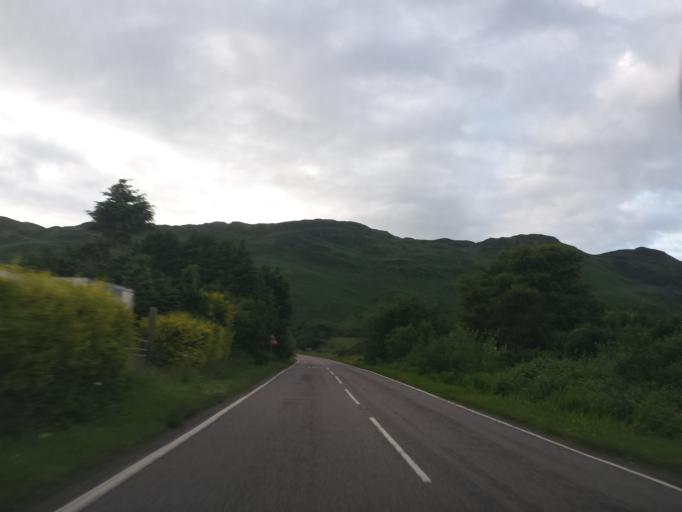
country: GB
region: Scotland
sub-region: Highland
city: Fort William
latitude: 57.2817
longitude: -5.5228
